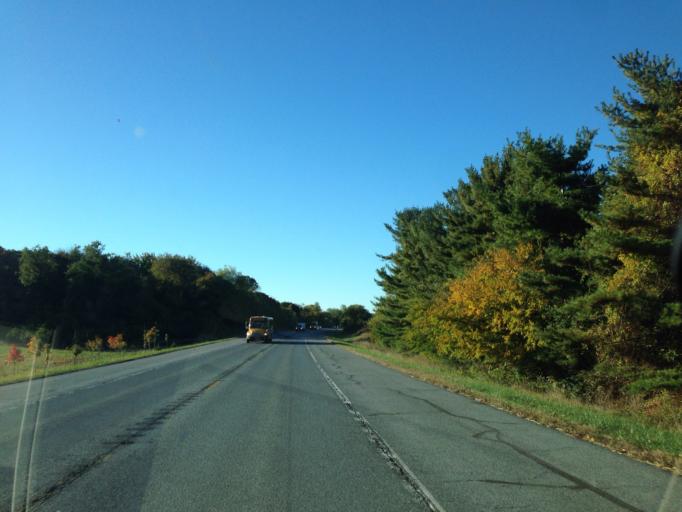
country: US
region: Maryland
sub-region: Carroll County
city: Mount Airy
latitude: 39.3858
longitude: -77.1415
